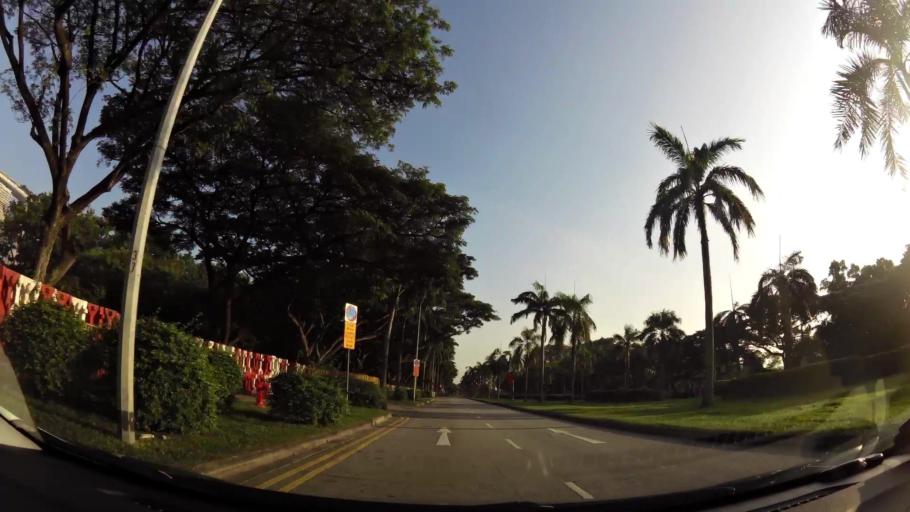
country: SG
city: Singapore
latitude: 1.2773
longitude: 103.8645
